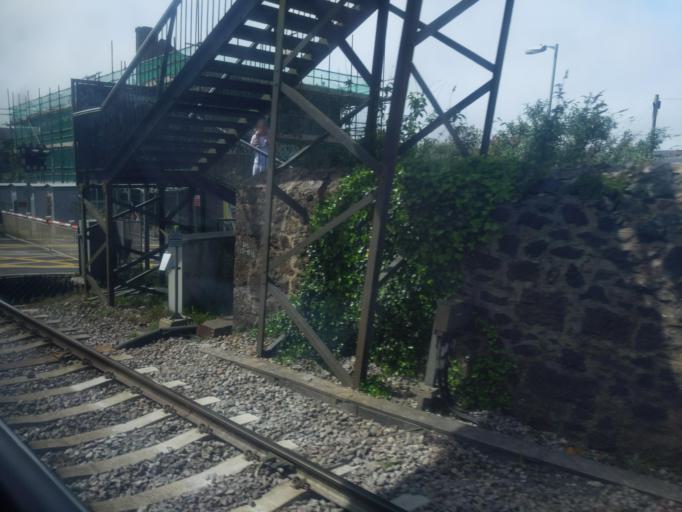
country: GB
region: England
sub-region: Cornwall
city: Camborne
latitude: 50.2144
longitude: -5.2830
